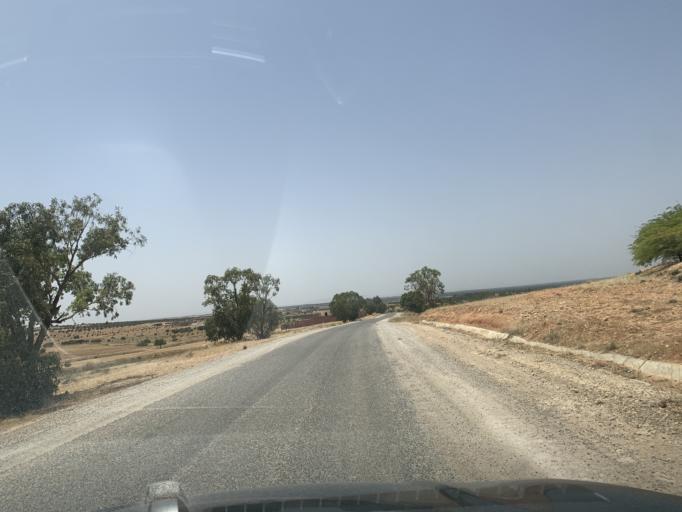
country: TN
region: Al Mahdiyah
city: Shurban
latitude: 35.1610
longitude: 10.2493
